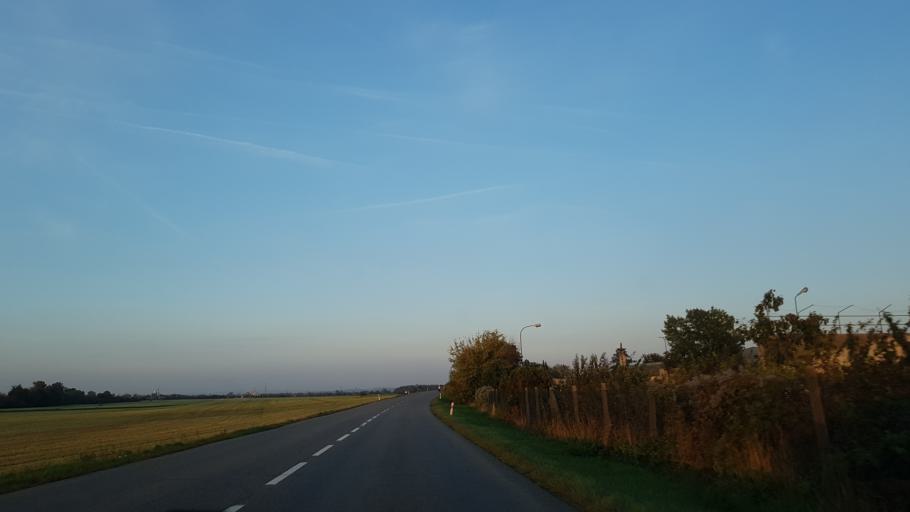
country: CZ
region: Zlin
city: Nedakonice
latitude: 49.0399
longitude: 17.3865
